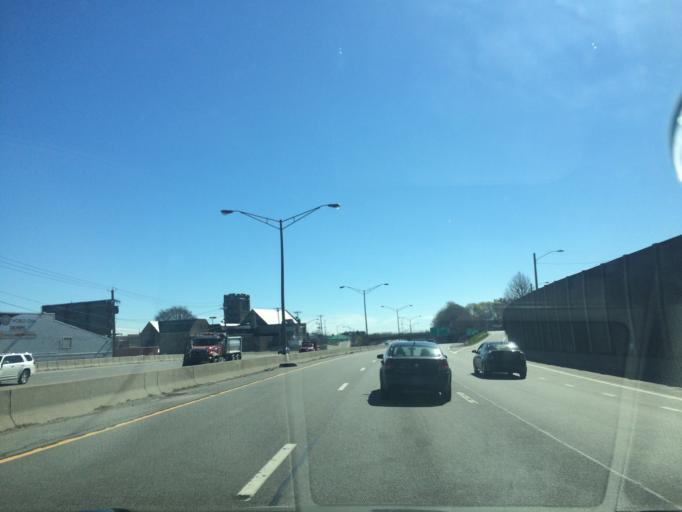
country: US
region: New York
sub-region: Monroe County
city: Brighton
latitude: 43.1448
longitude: -77.5600
